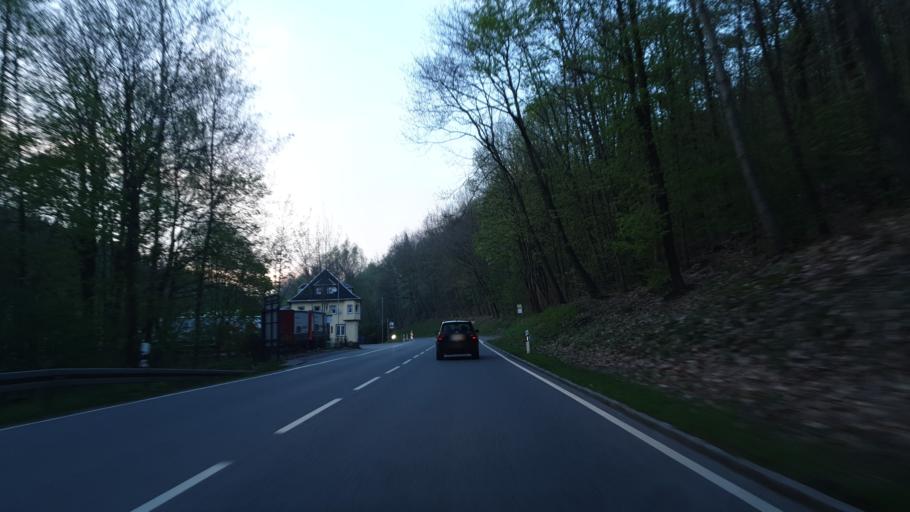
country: DE
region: Saxony
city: Aue
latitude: 50.6020
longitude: 12.7175
